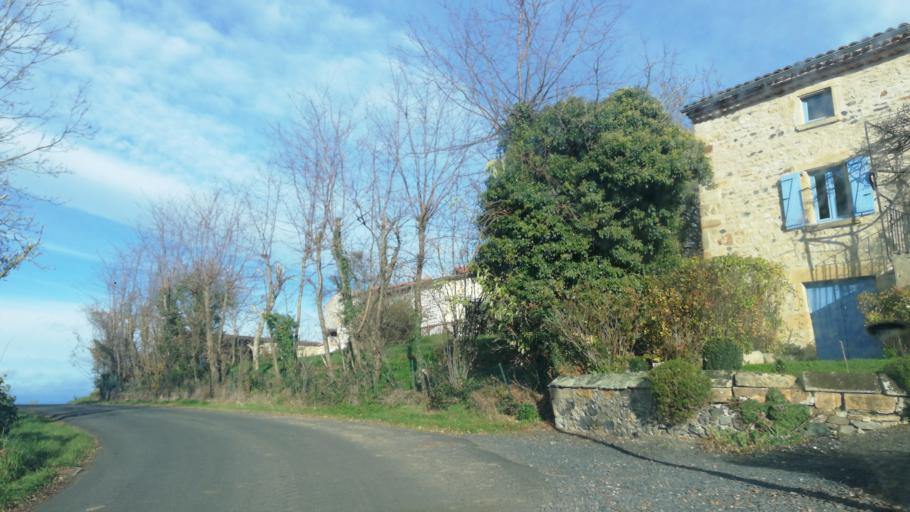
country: FR
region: Auvergne
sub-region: Departement du Puy-de-Dome
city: Billom
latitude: 45.6938
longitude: 3.3594
